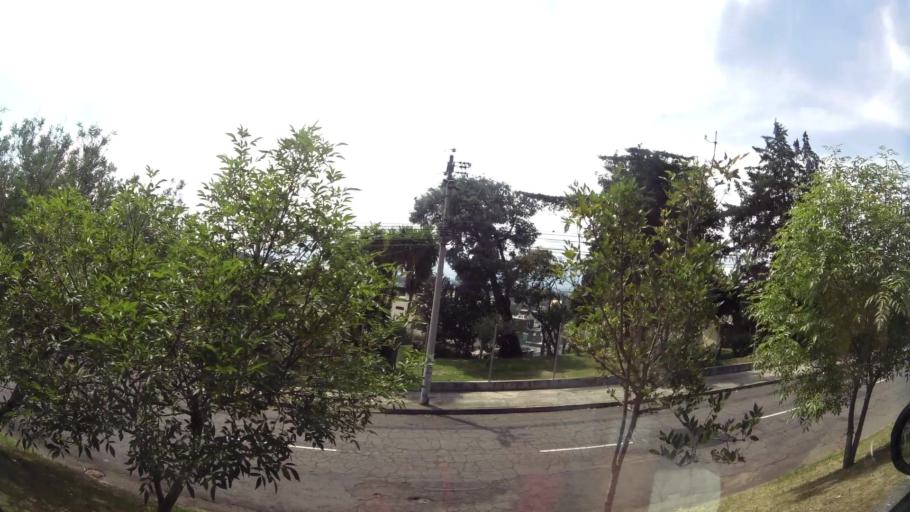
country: EC
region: Pichincha
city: Quito
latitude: -0.2086
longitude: -78.4284
